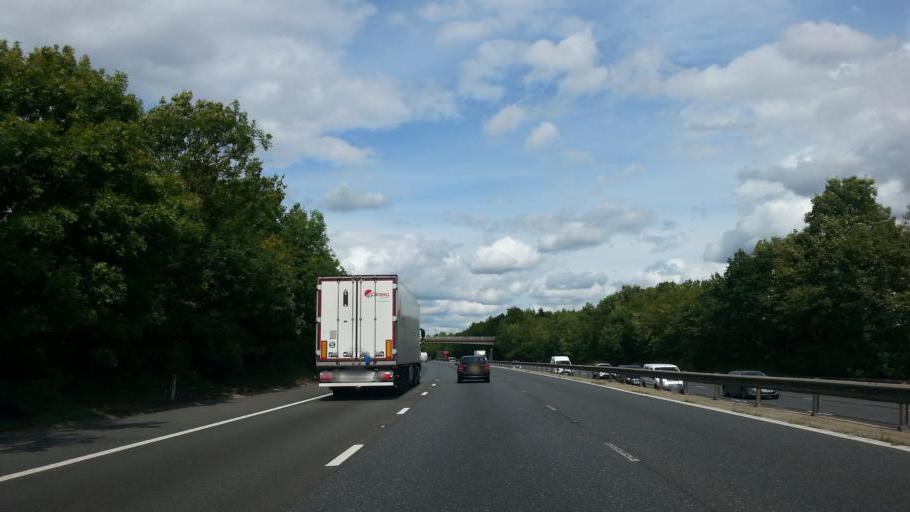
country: GB
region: England
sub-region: Essex
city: Little Hallingbury
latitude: 51.8326
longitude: 0.1927
